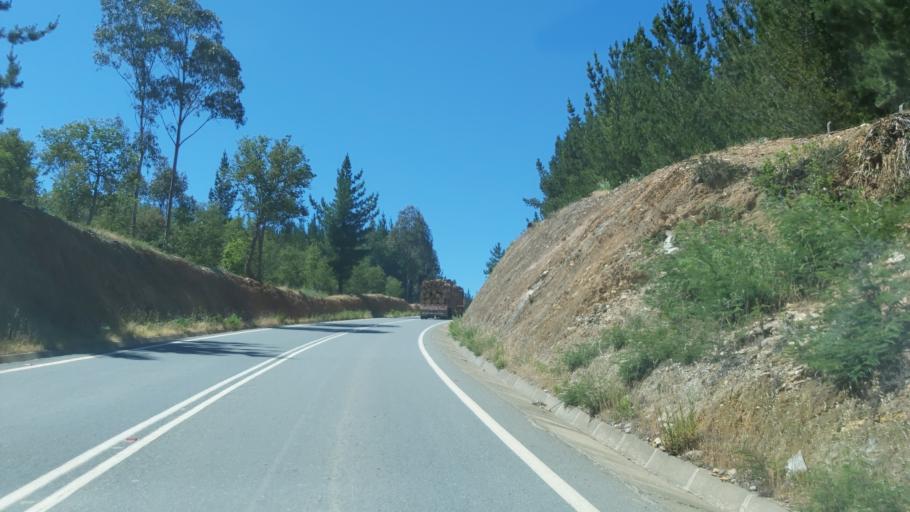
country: CL
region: Maule
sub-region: Provincia de Talca
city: Constitucion
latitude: -34.9246
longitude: -71.9881
